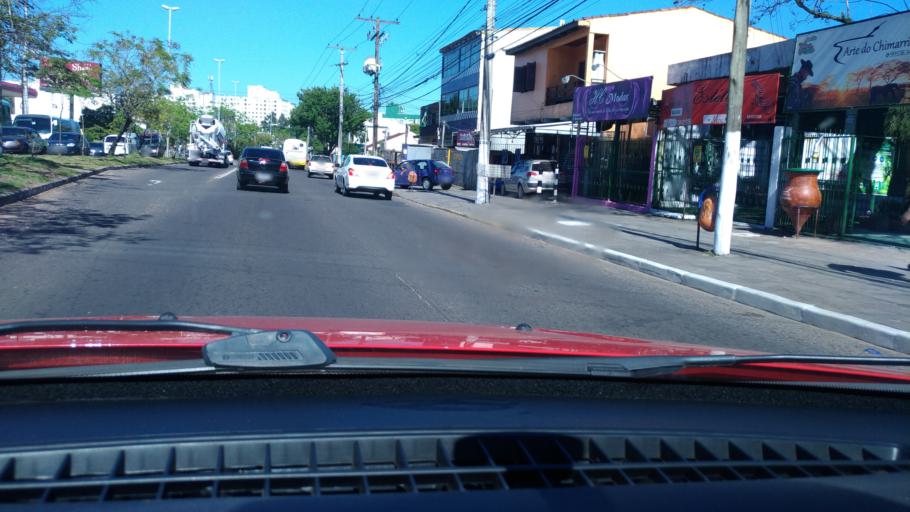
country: BR
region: Rio Grande do Sul
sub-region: Cachoeirinha
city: Cachoeirinha
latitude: -30.0392
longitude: -51.1242
